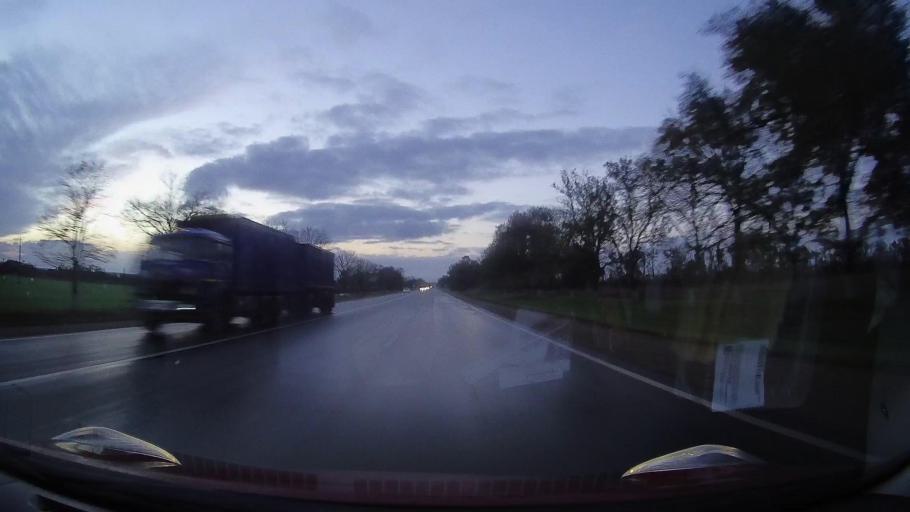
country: RU
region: Krasnodarskiy
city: Zavetnyy
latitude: 44.8960
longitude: 41.1953
